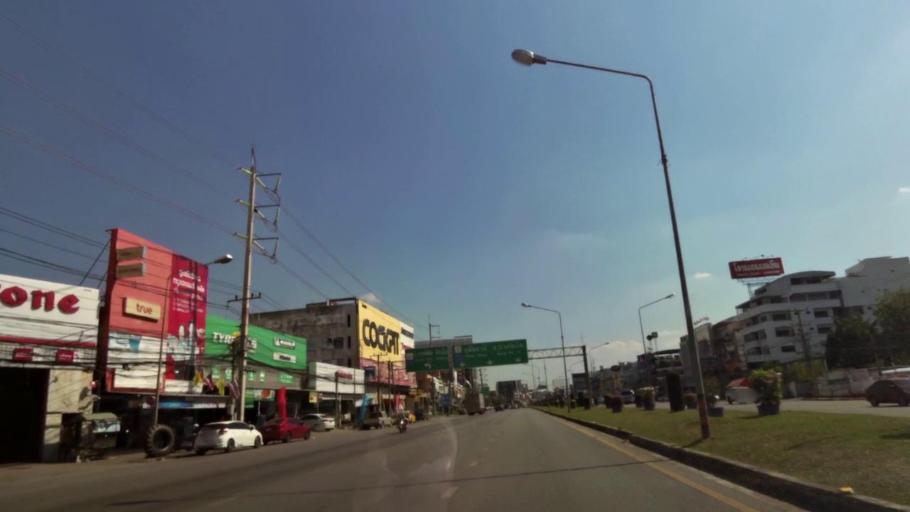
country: TH
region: Nakhon Sawan
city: Nakhon Sawan
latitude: 15.7005
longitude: 100.1182
